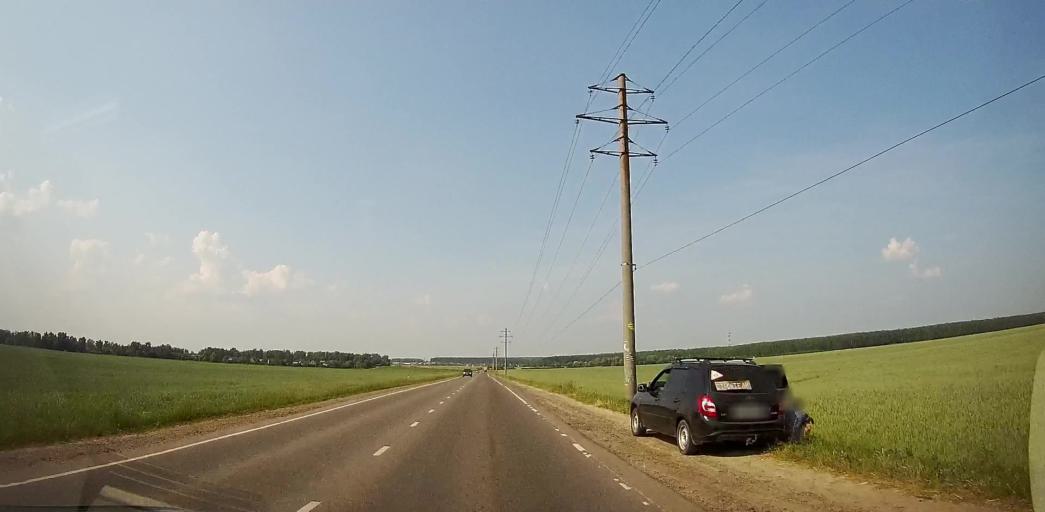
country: RU
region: Moskovskaya
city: Barybino
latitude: 55.2546
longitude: 37.9186
